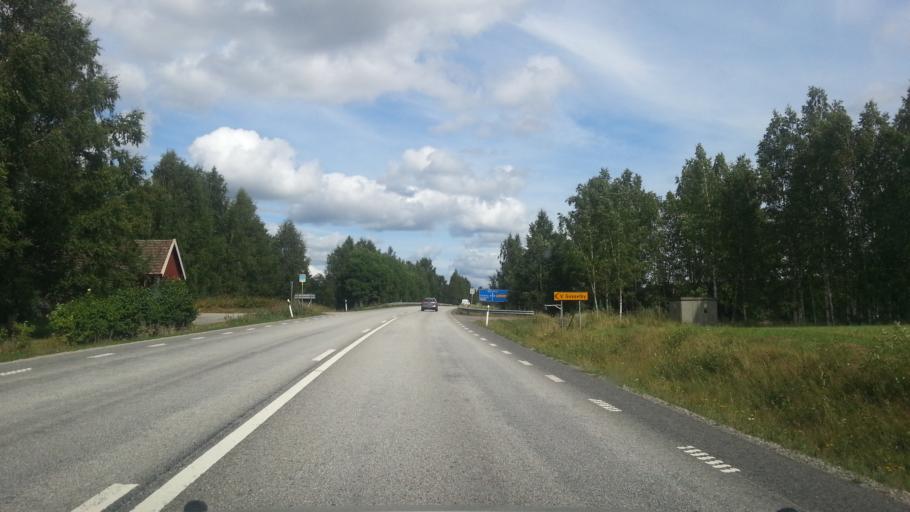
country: SE
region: OErebro
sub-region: Lindesbergs Kommun
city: Lindesberg
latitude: 59.6351
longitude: 15.2180
